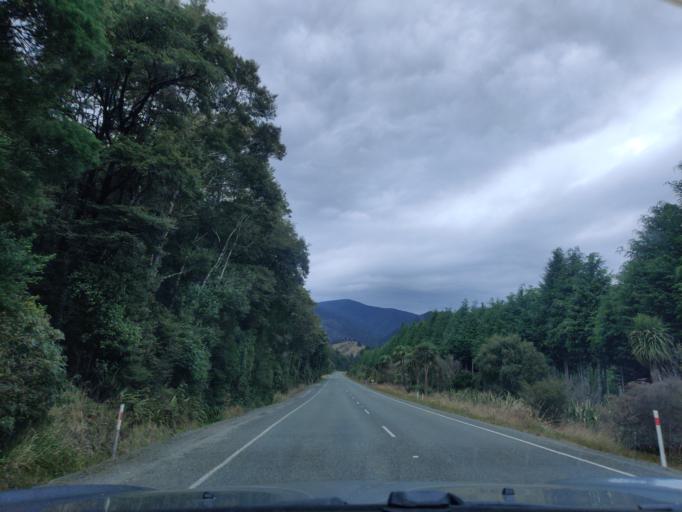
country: NZ
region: Tasman
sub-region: Tasman District
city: Wakefield
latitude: -41.6945
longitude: 172.4814
